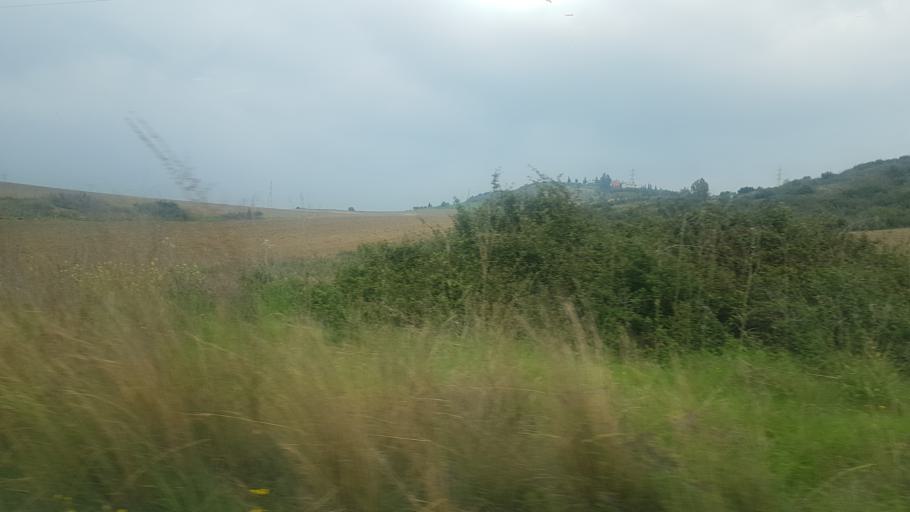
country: TR
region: Mersin
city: Yenice
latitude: 37.0553
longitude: 35.1694
